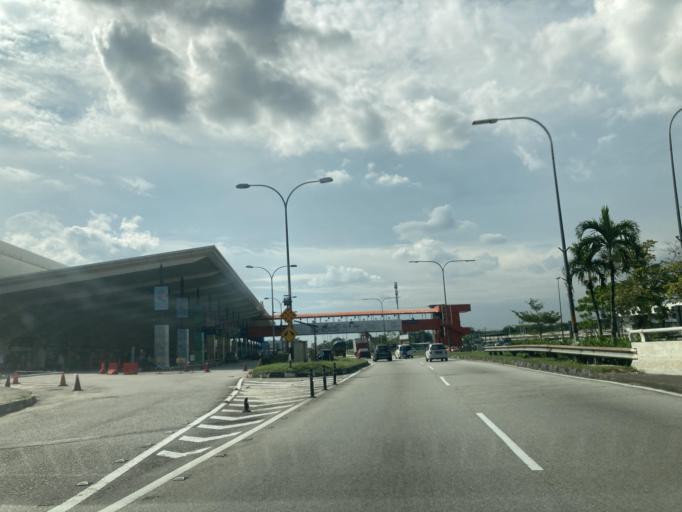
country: MY
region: Selangor
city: Kampung Baru Subang
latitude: 3.1323
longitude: 101.5548
